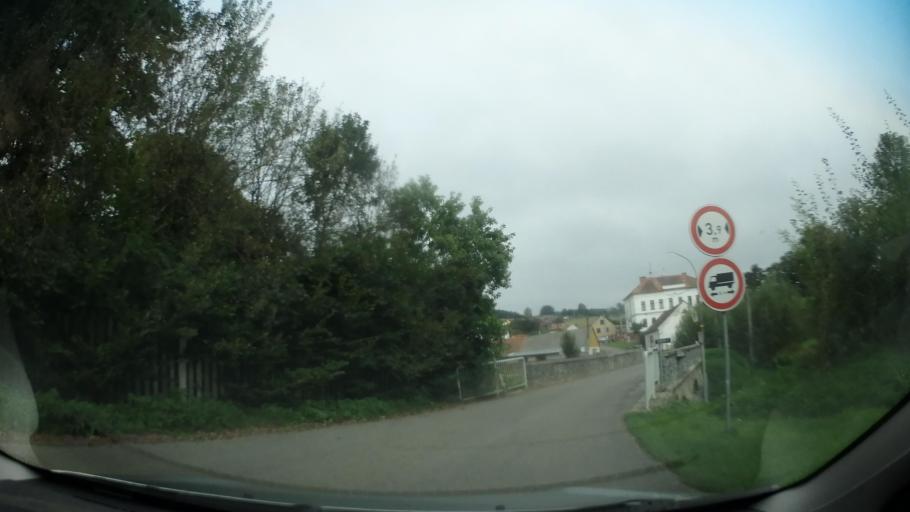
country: CZ
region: Central Bohemia
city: Sedlcany
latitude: 49.7147
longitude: 14.4141
